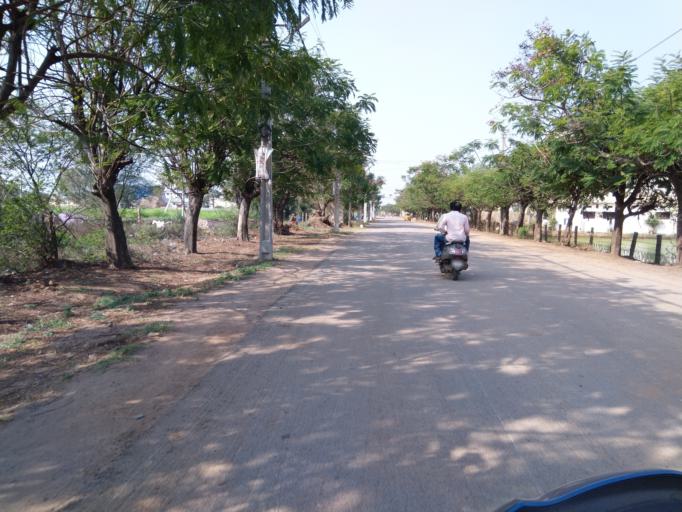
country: IN
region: Telangana
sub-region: Rangareddi
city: Quthbullapur
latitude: 17.5885
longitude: 78.4186
